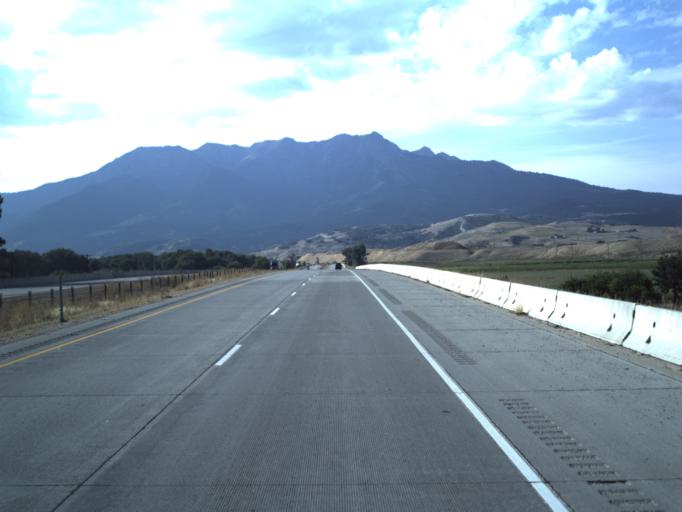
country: US
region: Utah
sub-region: Morgan County
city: Mountain Green
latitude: 41.1306
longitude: -111.7761
